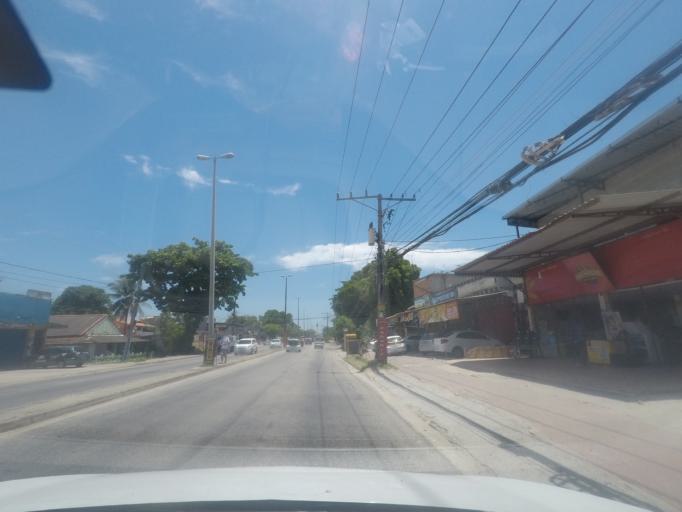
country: BR
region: Rio de Janeiro
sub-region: Itaguai
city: Itaguai
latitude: -22.9054
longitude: -43.6839
